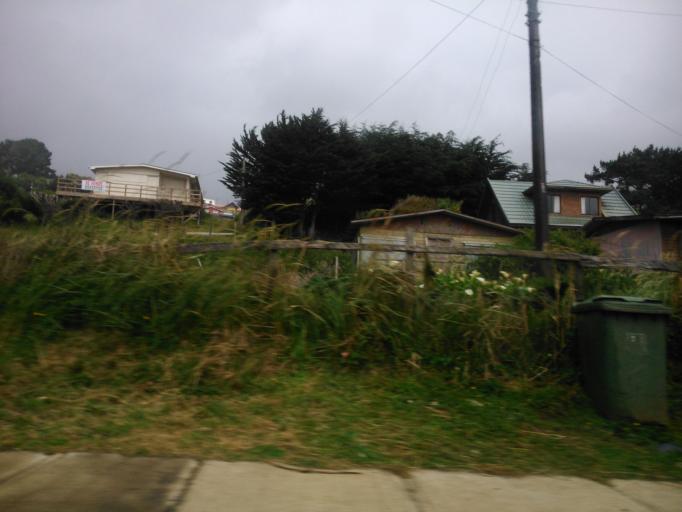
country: CL
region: Araucania
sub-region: Provincia de Cautin
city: Carahue
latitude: -38.8110
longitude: -73.3987
